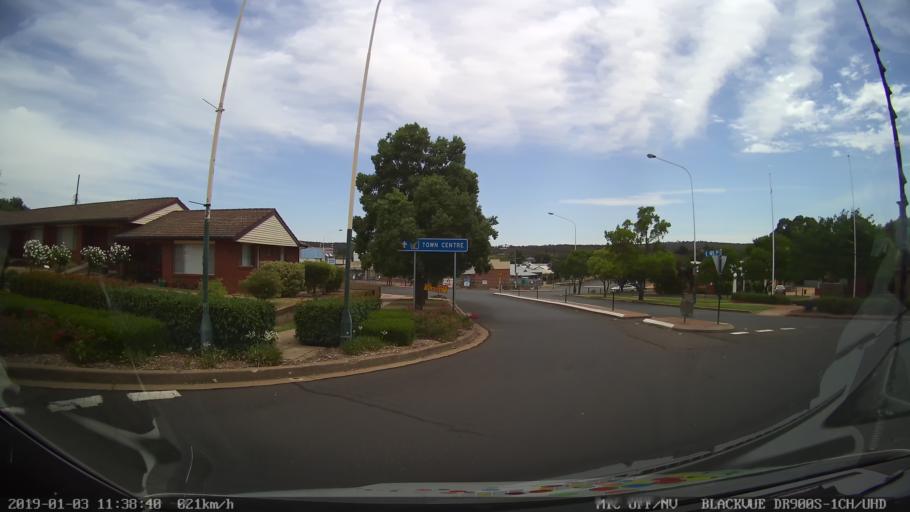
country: AU
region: New South Wales
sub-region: Weddin
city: Grenfell
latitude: -33.8951
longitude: 148.1626
